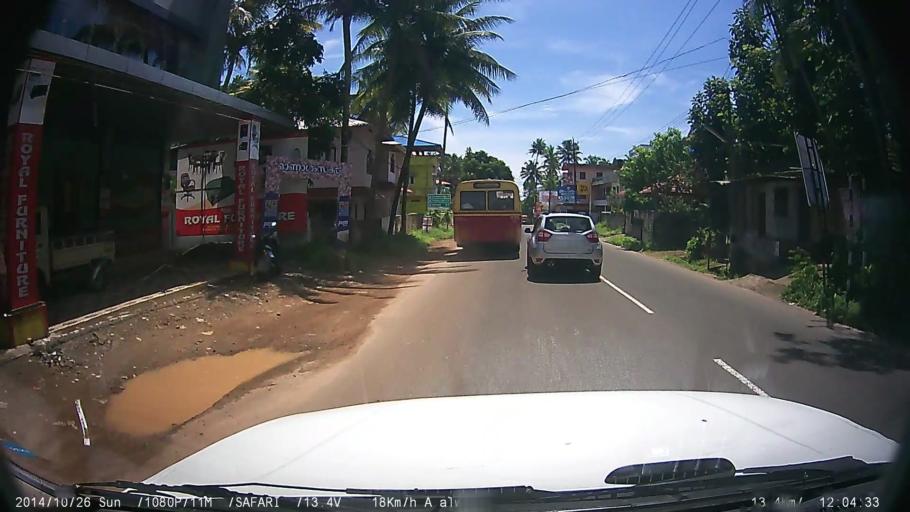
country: IN
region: Kerala
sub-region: Kottayam
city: Palackattumala
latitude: 9.6846
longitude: 76.5570
